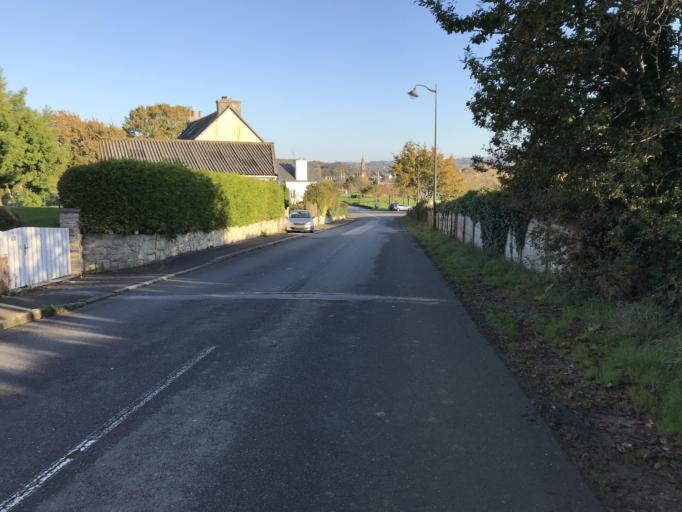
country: FR
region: Brittany
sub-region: Departement du Finistere
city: Le Faou
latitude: 48.2975
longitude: -4.1894
